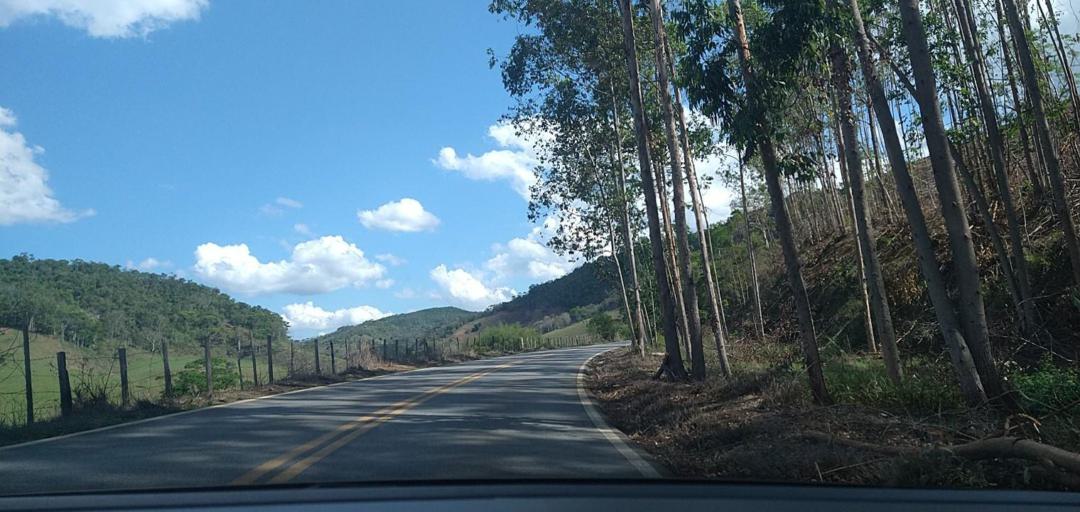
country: BR
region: Minas Gerais
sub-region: Rio Piracicaba
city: Rio Piracicaba
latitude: -19.9821
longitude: -43.1228
